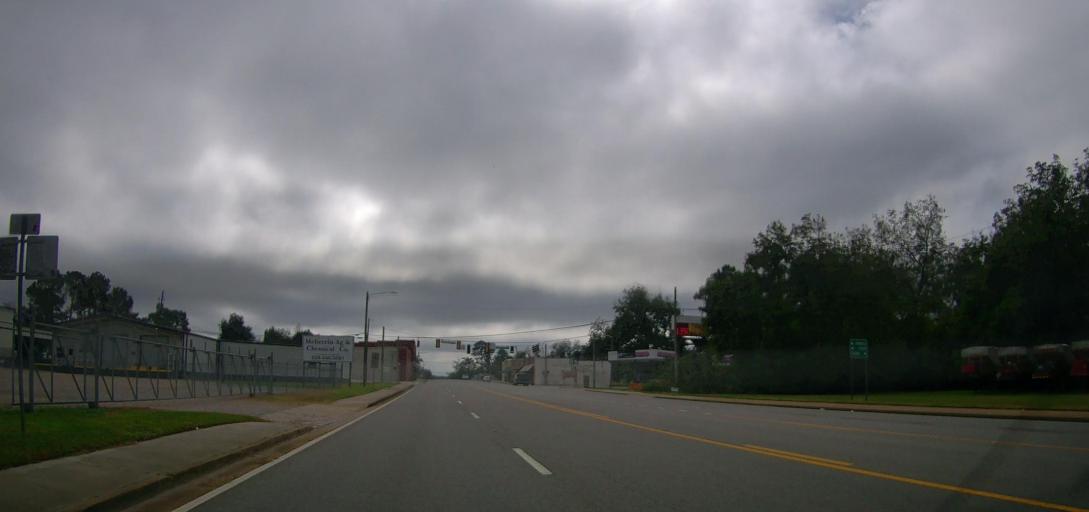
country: US
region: Georgia
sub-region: Colquitt County
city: Moultrie
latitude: 31.0124
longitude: -83.8662
